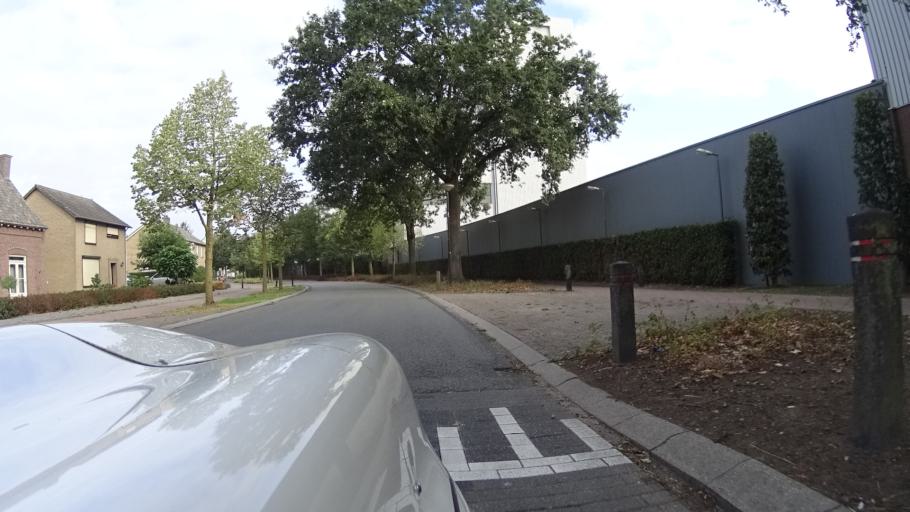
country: NL
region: Limburg
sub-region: Gemeente Venray
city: Venray
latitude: 51.5682
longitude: 6.0366
